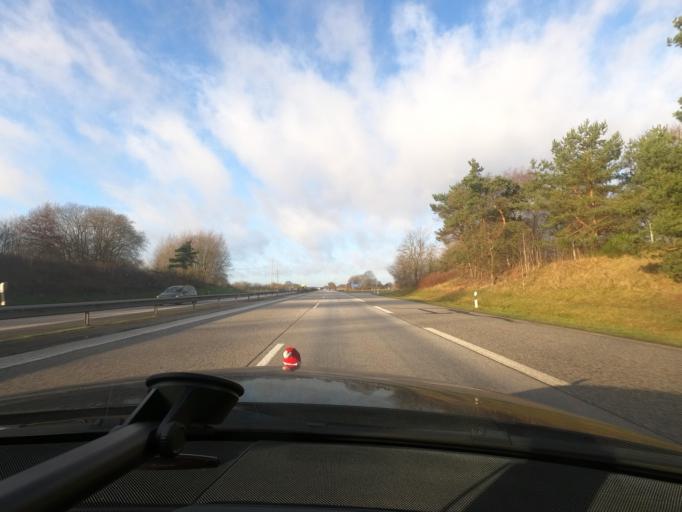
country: DE
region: Schleswig-Holstein
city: Brekendorf
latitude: 54.4012
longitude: 9.6394
